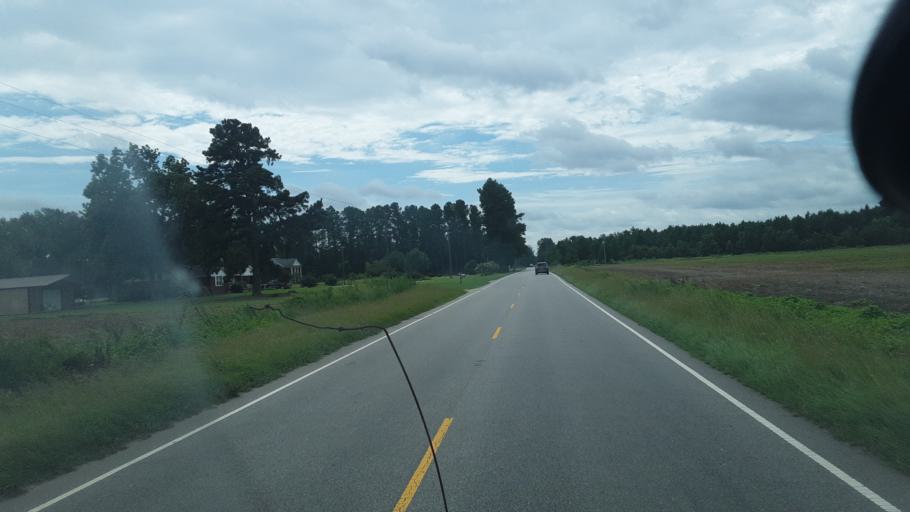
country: US
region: North Carolina
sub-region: Robeson County
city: Rowland
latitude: 34.6217
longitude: -79.3343
